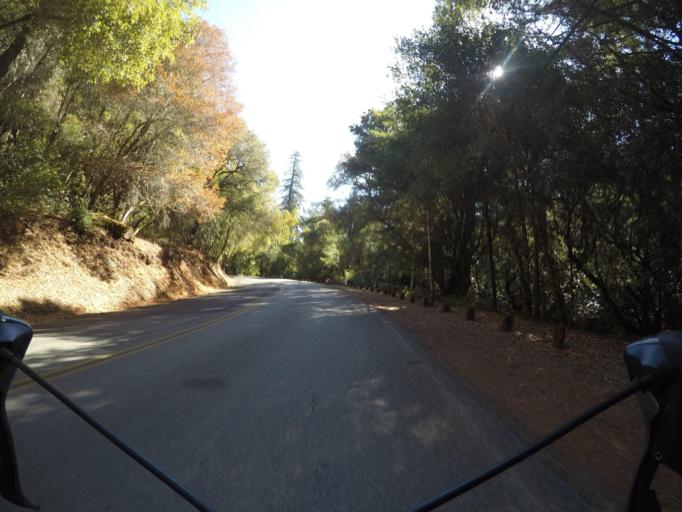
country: US
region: California
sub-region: San Mateo County
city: Portola Valley
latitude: 37.2763
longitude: -122.2908
